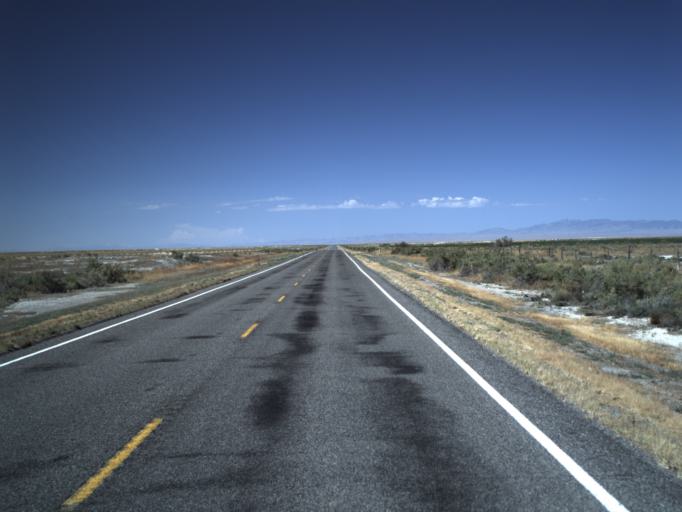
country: US
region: Utah
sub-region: Millard County
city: Delta
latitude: 39.3273
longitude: -112.7274
